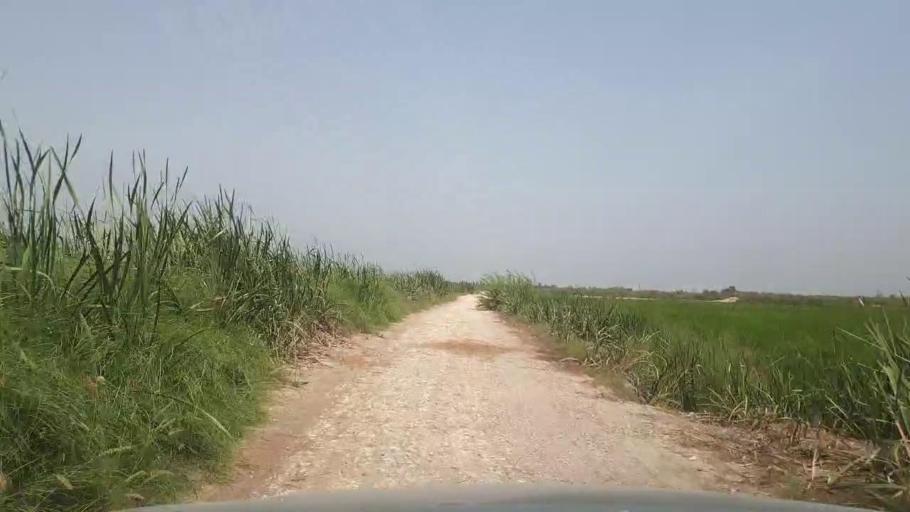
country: PK
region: Sindh
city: Garhi Yasin
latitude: 27.9469
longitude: 68.4294
